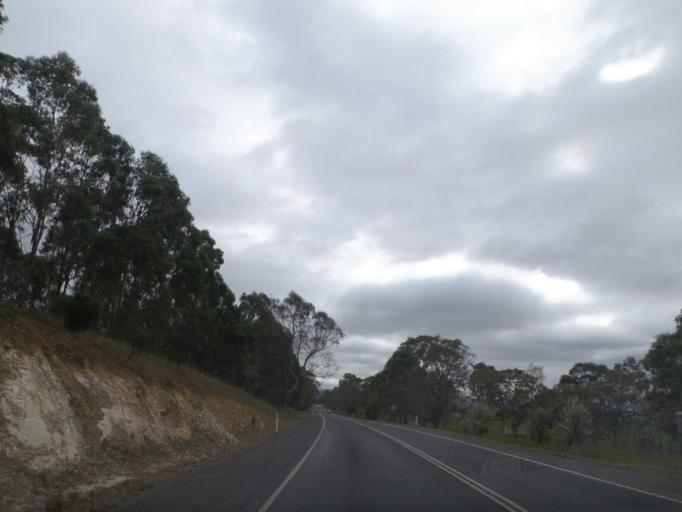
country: AU
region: Victoria
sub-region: Whittlesea
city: Mernda
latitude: -37.5645
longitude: 145.1091
